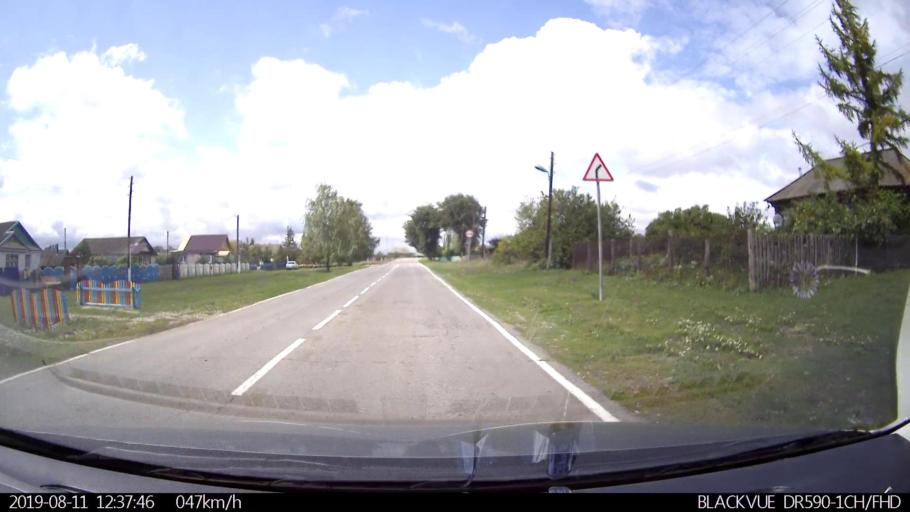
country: RU
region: Ulyanovsk
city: Ignatovka
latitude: 53.8243
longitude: 47.8114
